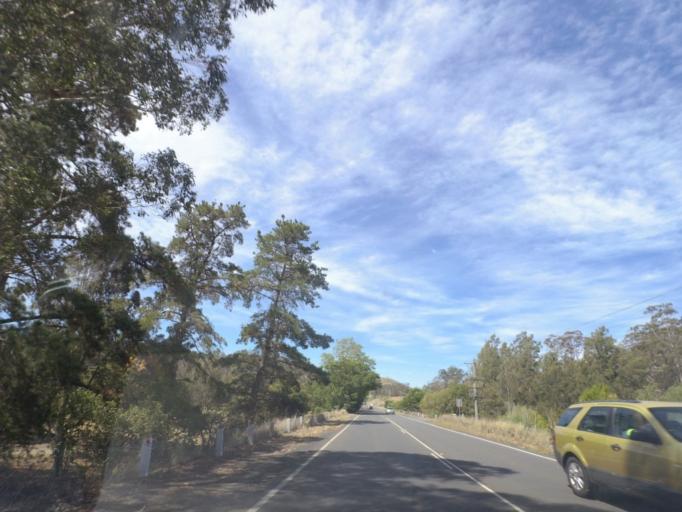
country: AU
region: New South Wales
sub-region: Wollondilly
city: Picton
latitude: -34.1667
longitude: 150.6292
